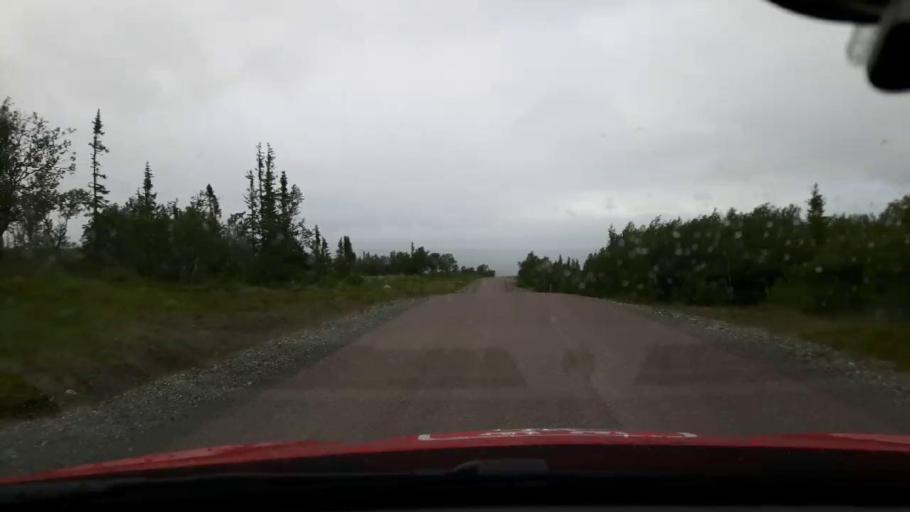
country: SE
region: Jaemtland
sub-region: Are Kommun
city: Are
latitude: 63.2383
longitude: 12.4306
